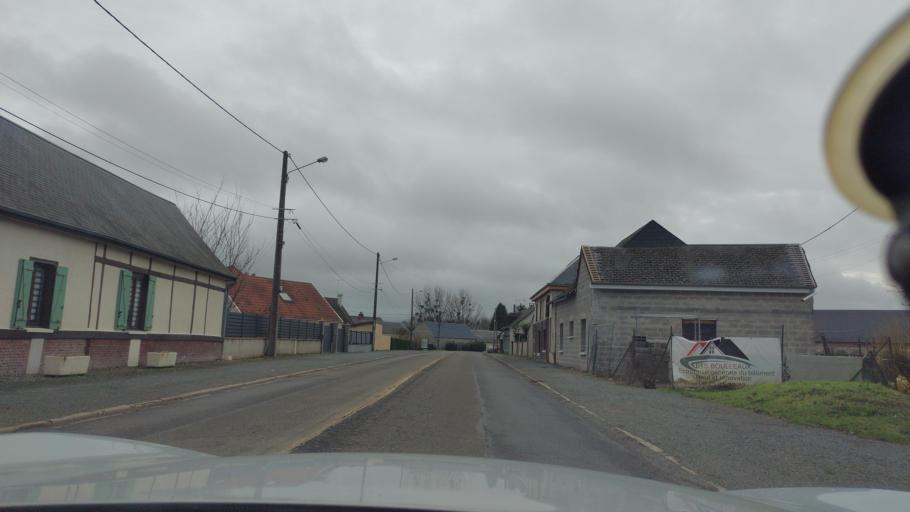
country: FR
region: Picardie
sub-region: Departement de l'Oise
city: Grandvilliers
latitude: 49.6347
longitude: 1.9464
